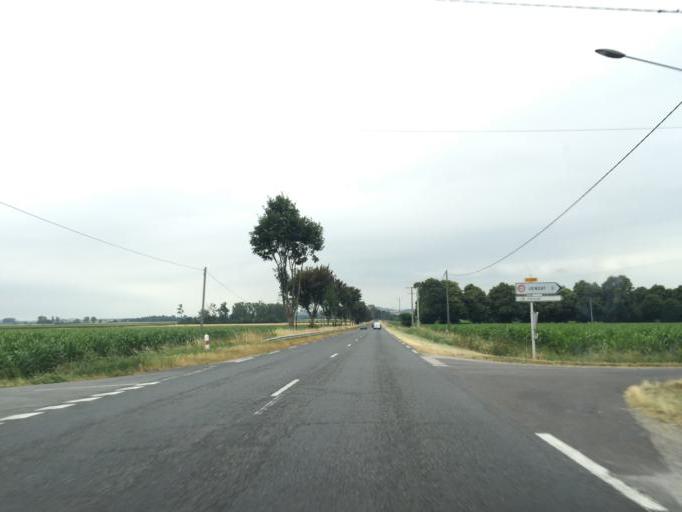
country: FR
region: Auvergne
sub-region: Departement de l'Allier
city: Brout-Vernet
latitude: 46.1604
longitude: 3.2341
